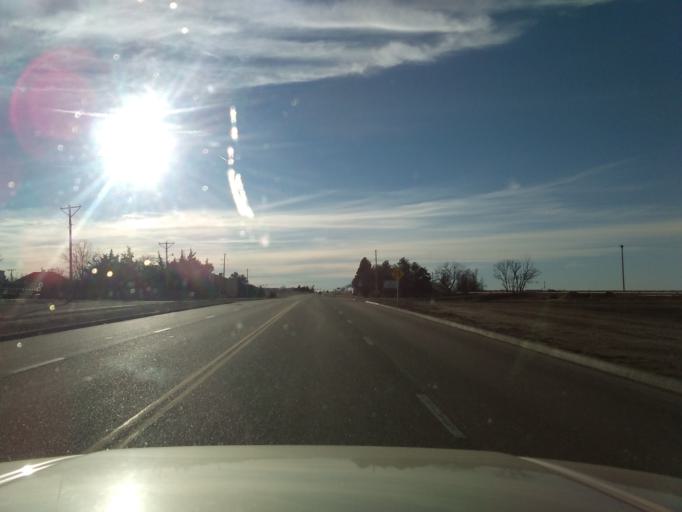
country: US
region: Kansas
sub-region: Sheridan County
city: Hoxie
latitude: 39.5432
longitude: -100.5697
